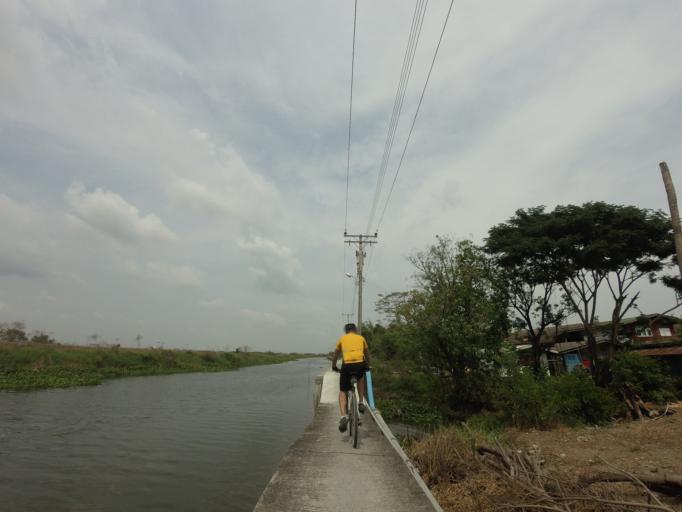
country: TH
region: Bangkok
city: Lat Krabang
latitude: 13.6964
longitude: 100.7758
